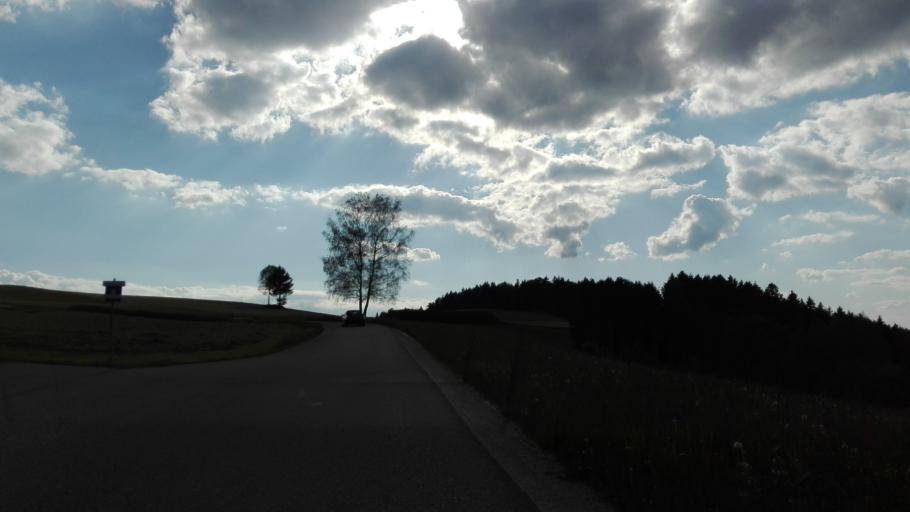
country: AT
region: Upper Austria
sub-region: Politischer Bezirk Perg
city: Bad Kreuzen
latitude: 48.4122
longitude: 14.7088
